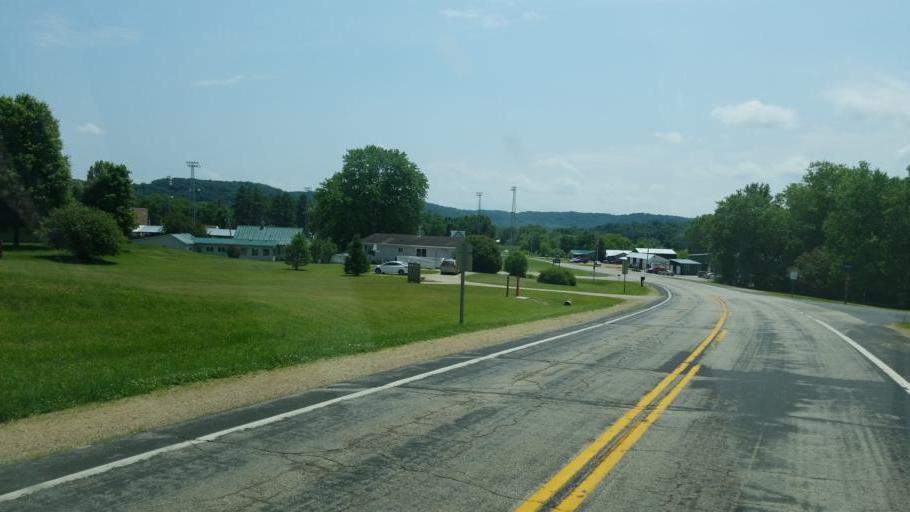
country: US
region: Wisconsin
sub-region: Monroe County
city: Cashton
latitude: 43.5815
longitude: -90.6406
